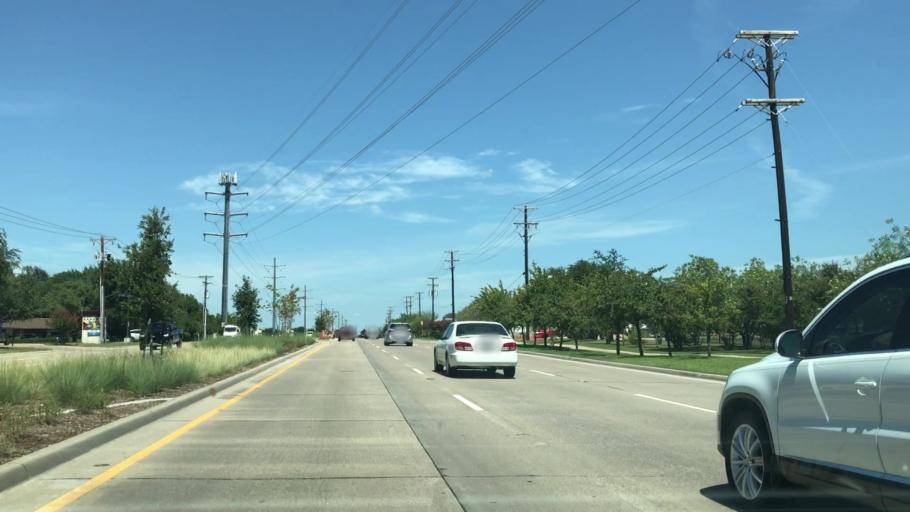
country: US
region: Texas
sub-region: Dallas County
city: Rowlett
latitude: 32.9122
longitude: -96.5283
